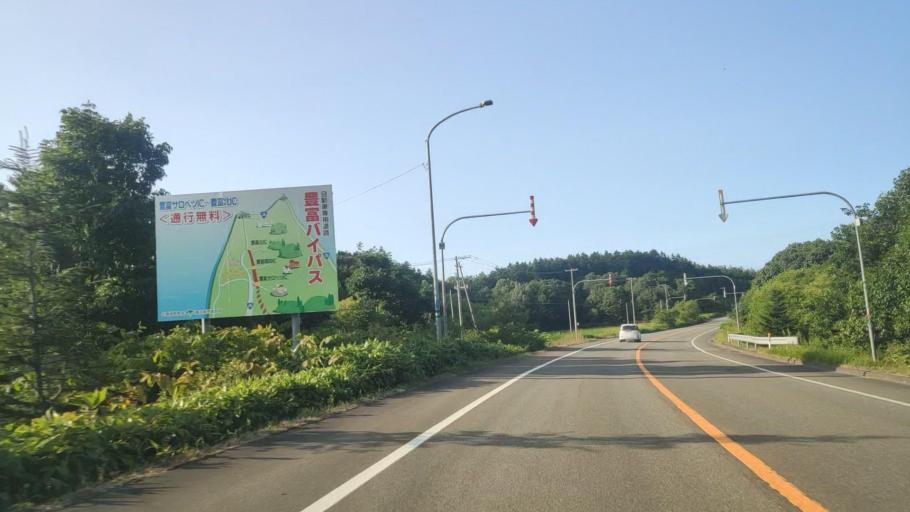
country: JP
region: Hokkaido
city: Makubetsu
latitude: 45.0792
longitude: 141.7534
